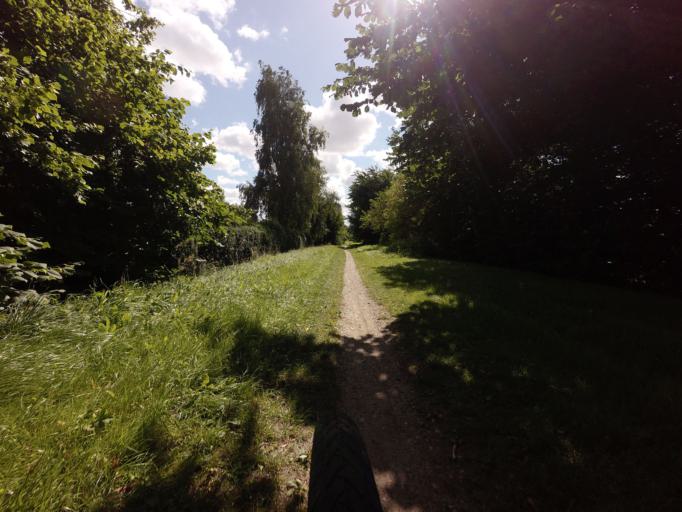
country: DK
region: Central Jutland
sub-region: Horsens Kommune
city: Horsens
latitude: 55.8938
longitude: 9.7733
